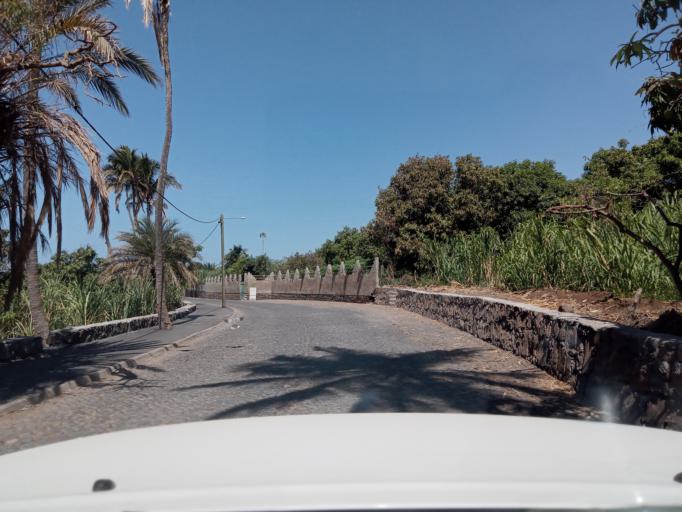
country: CV
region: Ribeira Grande de Santiago
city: Cidade Velha
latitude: 14.9158
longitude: -23.6115
